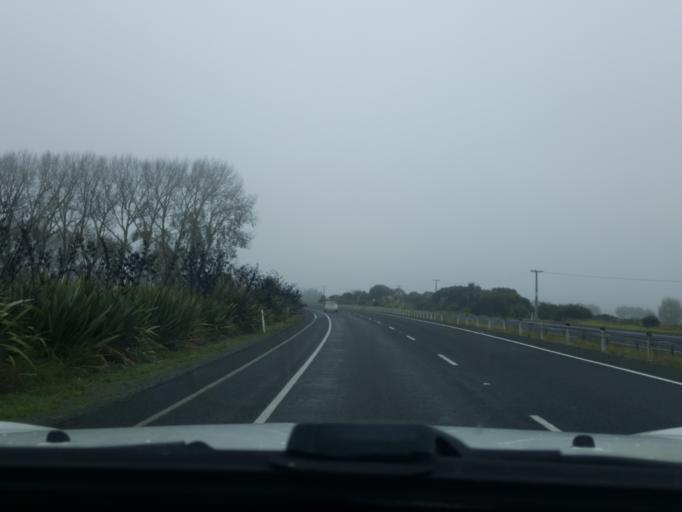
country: NZ
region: Waikato
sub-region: Waikato District
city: Te Kauwhata
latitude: -37.4463
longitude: 175.1518
